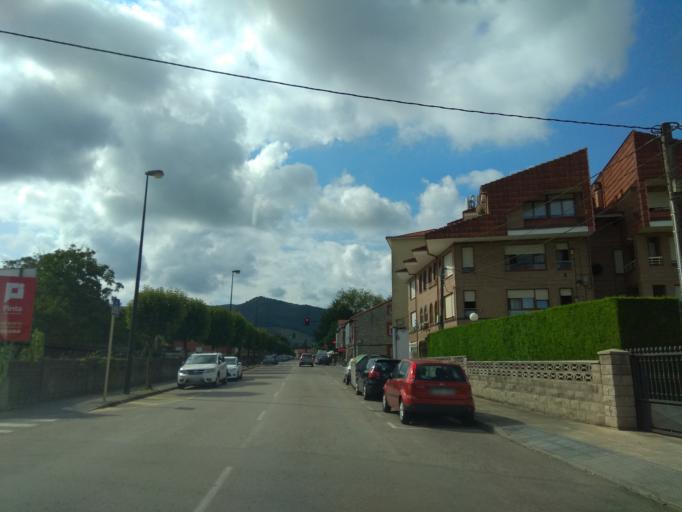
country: ES
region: Cantabria
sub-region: Provincia de Cantabria
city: Torrelavega
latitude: 43.3355
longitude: -4.0447
